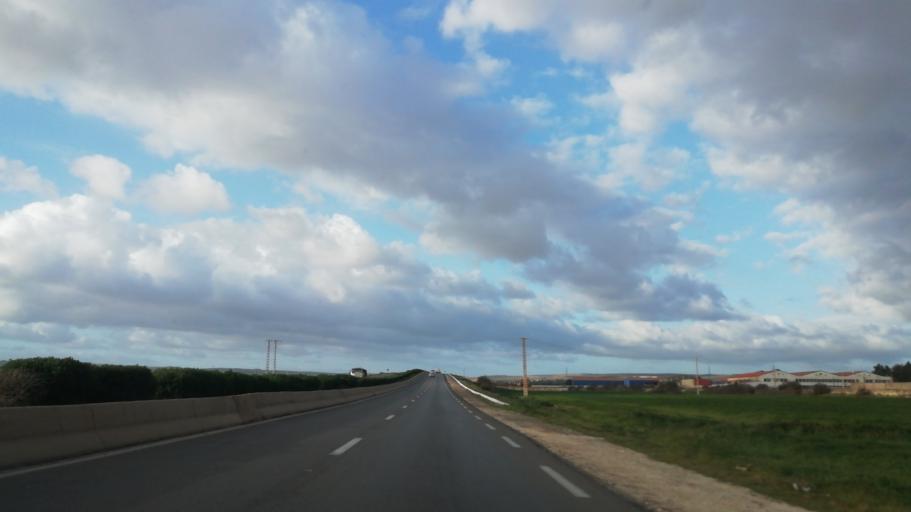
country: DZ
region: Ain Temouchent
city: El Amria
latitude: 35.5180
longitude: -1.0146
